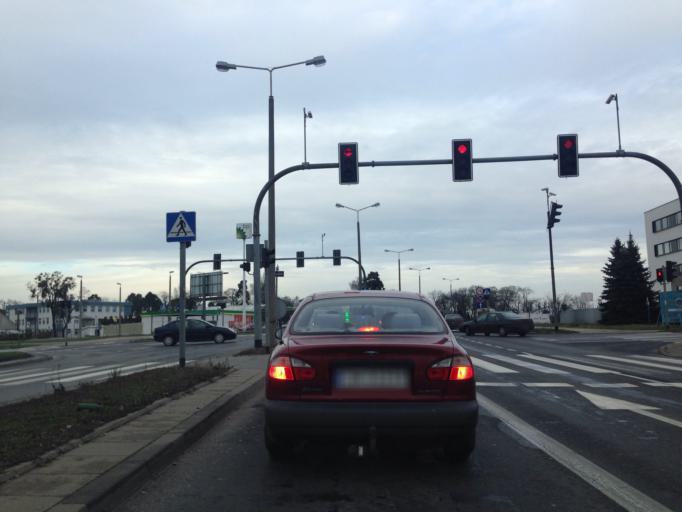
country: PL
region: Kujawsko-Pomorskie
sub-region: Torun
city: Torun
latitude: 53.0310
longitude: 18.6106
